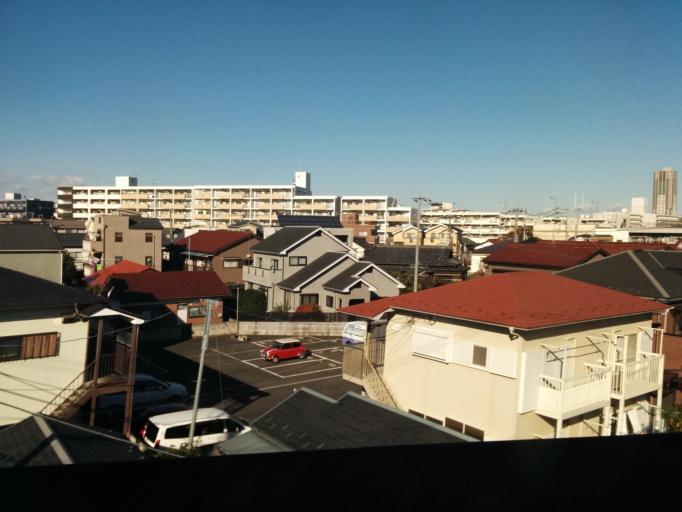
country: JP
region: Kanagawa
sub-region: Kawasaki-shi
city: Kawasaki
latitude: 35.5629
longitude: 139.6620
